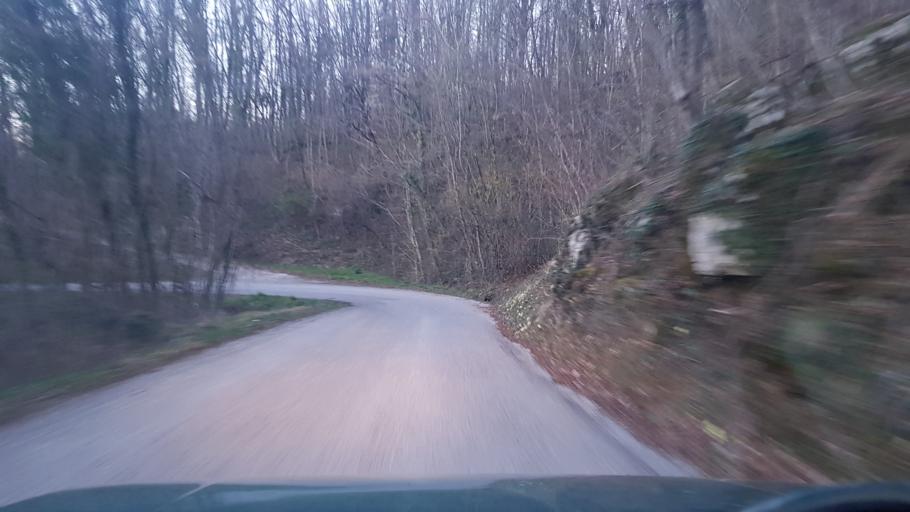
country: SI
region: Kanal
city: Kanal
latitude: 46.0793
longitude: 13.6475
